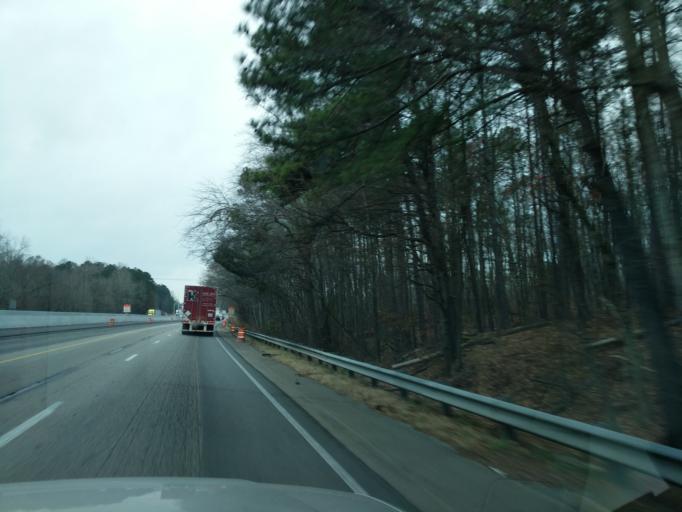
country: US
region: Georgia
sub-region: Gwinnett County
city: Buford
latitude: 34.0566
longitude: -83.9707
